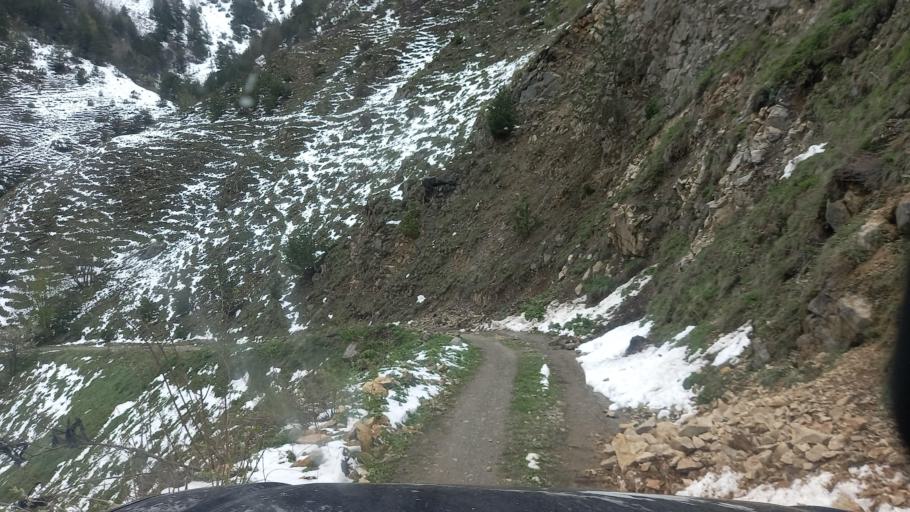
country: RU
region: North Ossetia
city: Mizur
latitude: 42.8029
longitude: 43.9351
